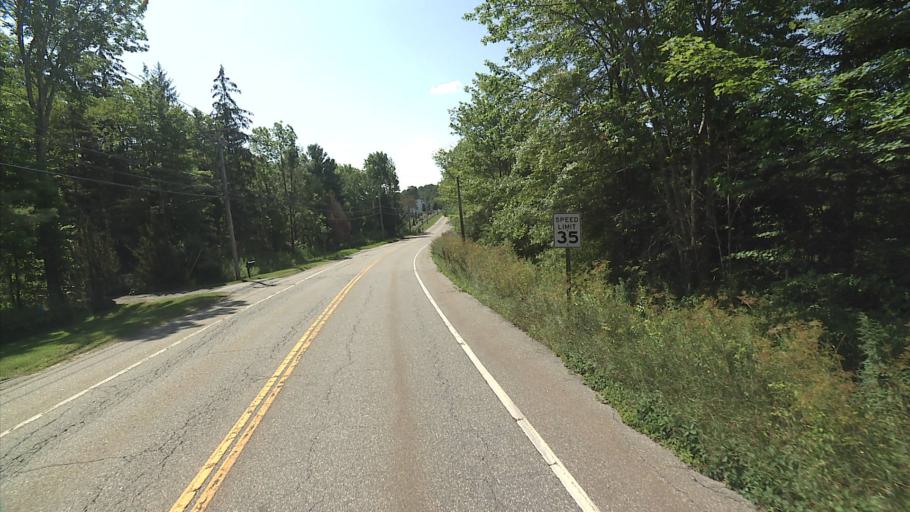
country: US
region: Connecticut
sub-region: Litchfield County
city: New Preston
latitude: 41.7484
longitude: -73.3499
